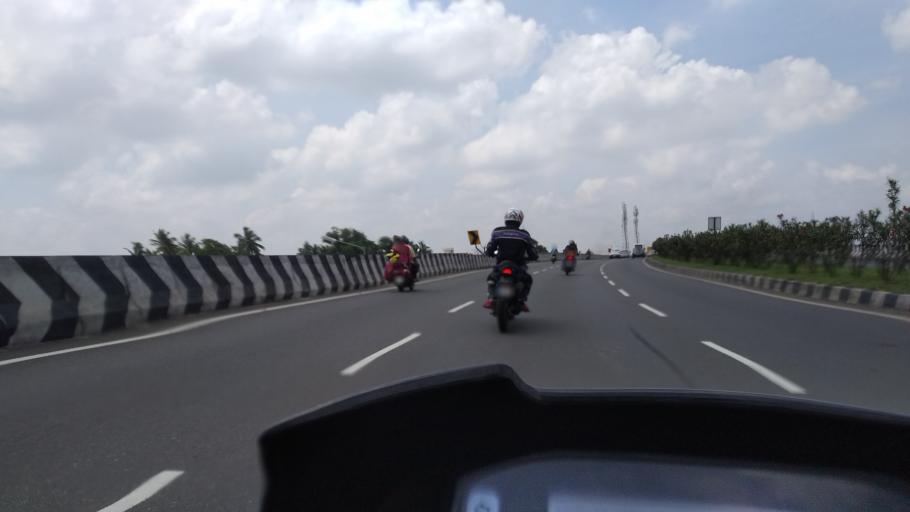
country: IN
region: Tamil Nadu
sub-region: Tiruppur
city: Avinashi
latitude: 11.1268
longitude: 77.1973
